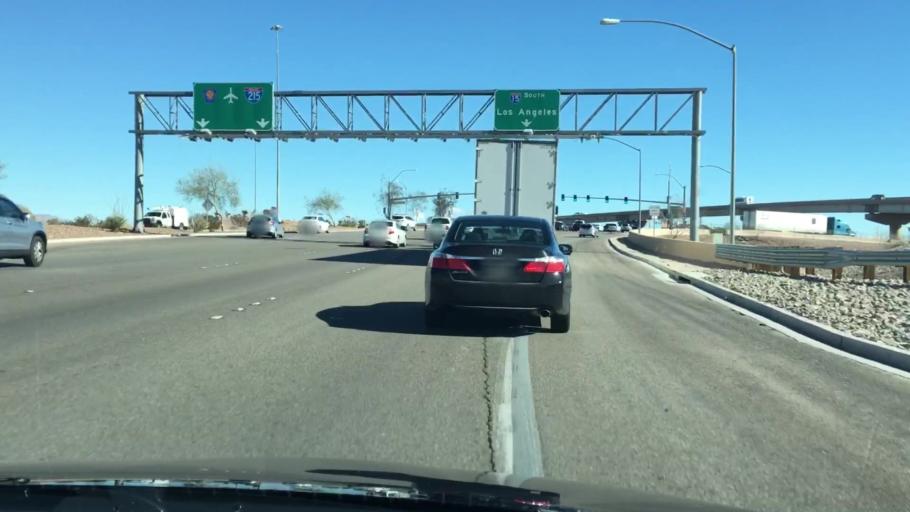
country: US
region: Nevada
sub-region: Clark County
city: Enterprise
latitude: 36.0431
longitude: -115.1832
